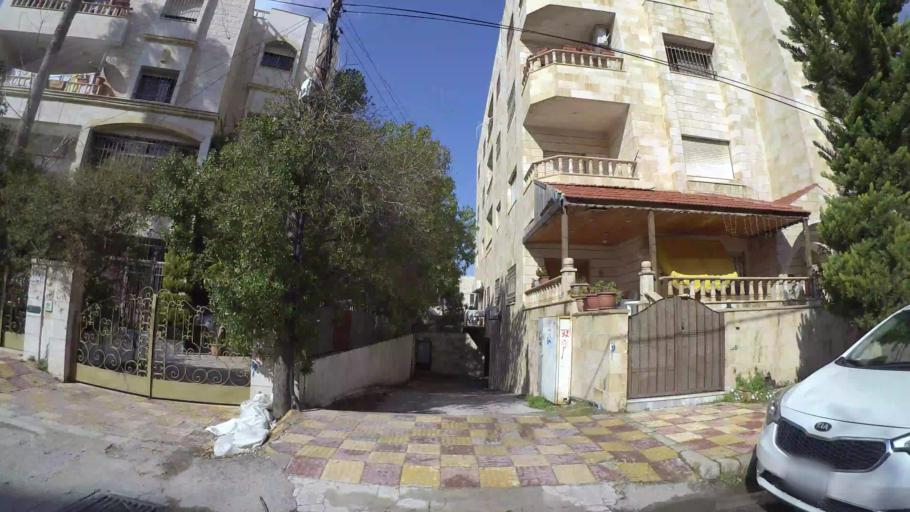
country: JO
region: Amman
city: Al Jubayhah
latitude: 31.9753
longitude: 35.8907
